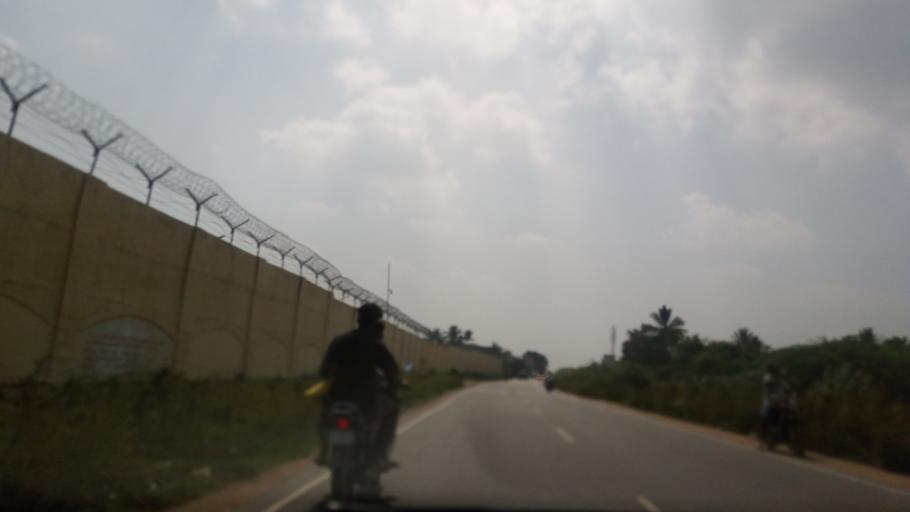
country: IN
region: Tamil Nadu
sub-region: Vellore
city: Arakkonam
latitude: 13.0600
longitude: 79.6740
